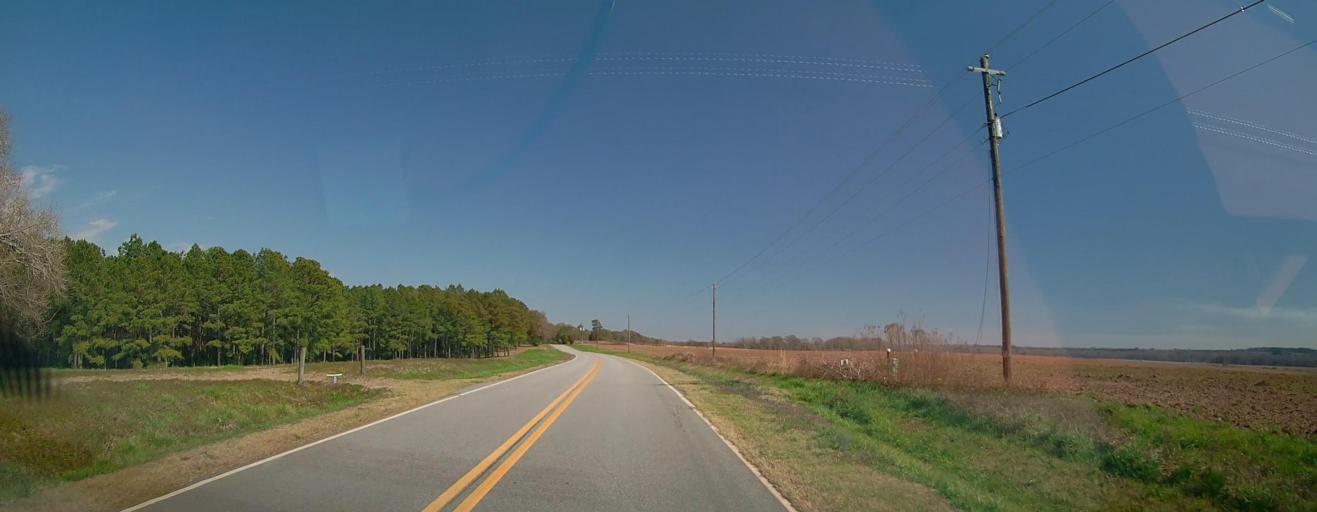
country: US
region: Georgia
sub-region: Houston County
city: Perry
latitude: 32.4385
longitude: -83.7349
